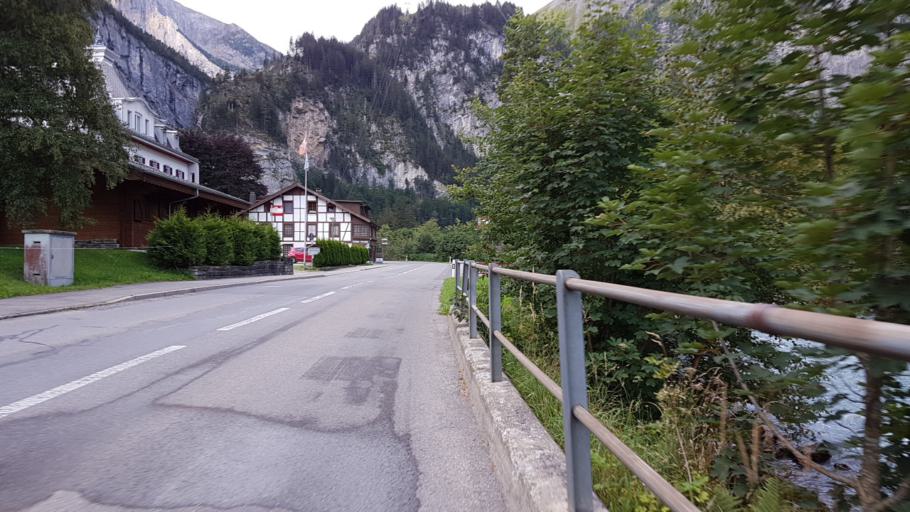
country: CH
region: Bern
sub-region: Frutigen-Niedersimmental District
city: Kandersteg
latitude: 46.4795
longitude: 7.6648
